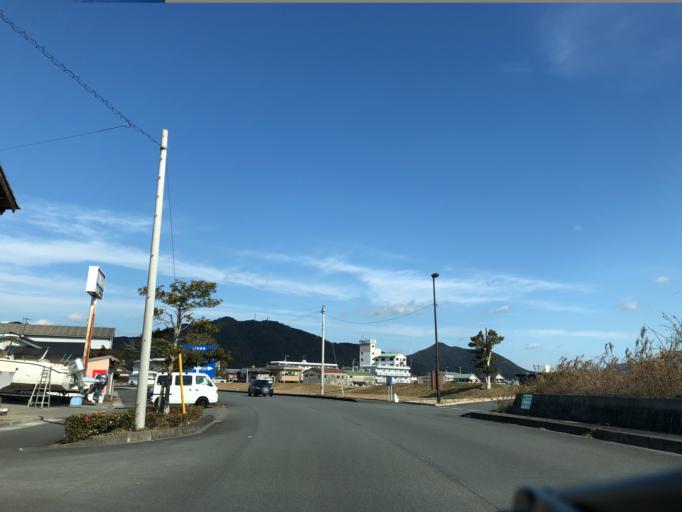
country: JP
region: Kochi
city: Sukumo
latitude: 32.9236
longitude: 132.7026
